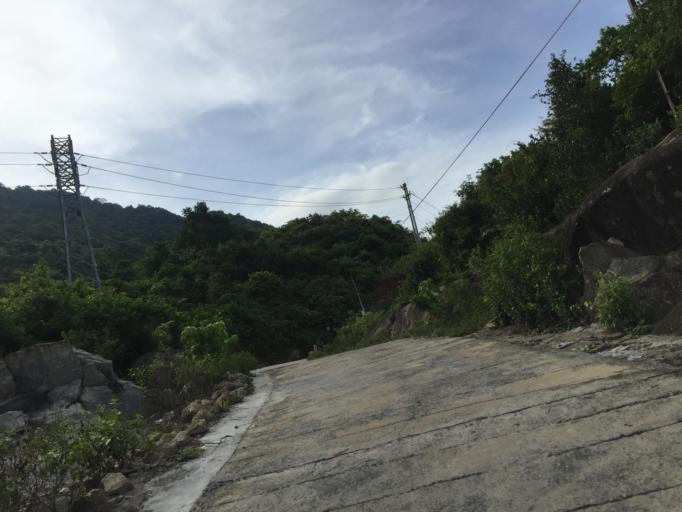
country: VN
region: Quang Nam
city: Hoi An
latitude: 15.9536
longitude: 108.5084
